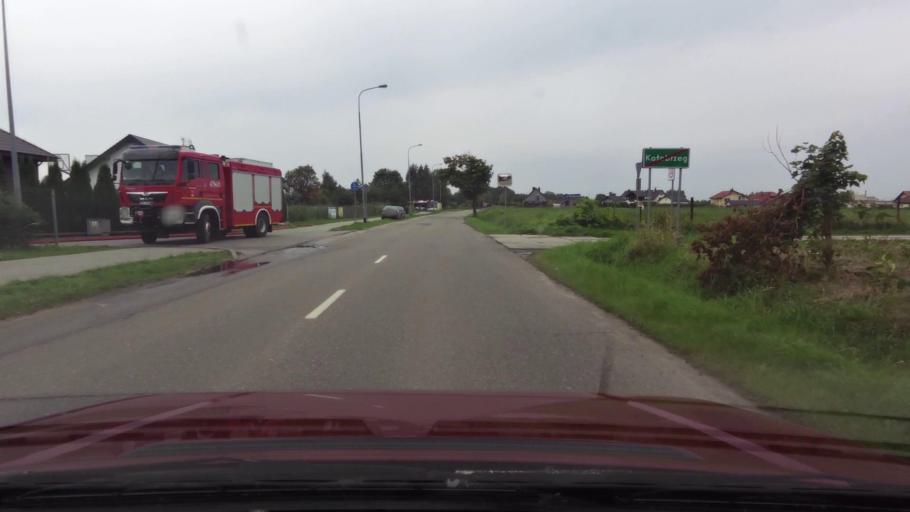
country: PL
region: West Pomeranian Voivodeship
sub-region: Powiat kolobrzeski
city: Kolobrzeg
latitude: 54.1537
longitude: 15.5413
